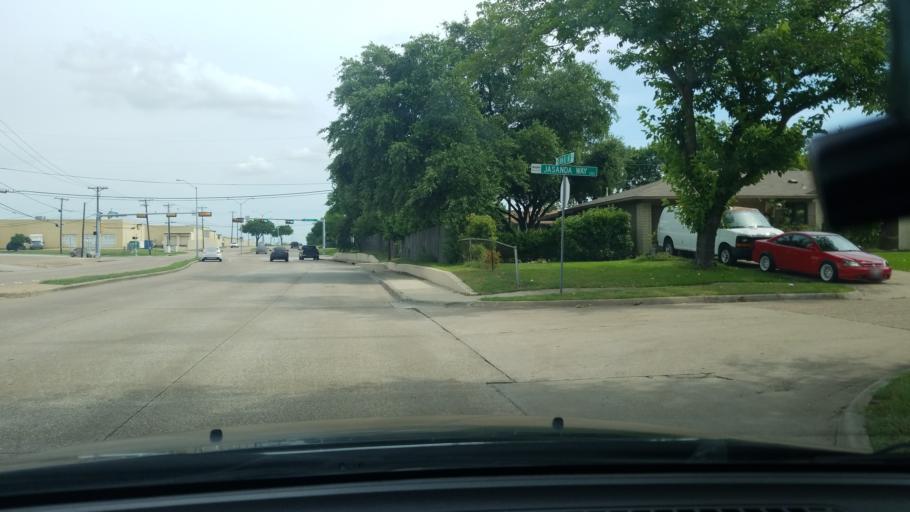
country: US
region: Texas
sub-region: Dallas County
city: Mesquite
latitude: 32.7692
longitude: -96.5969
